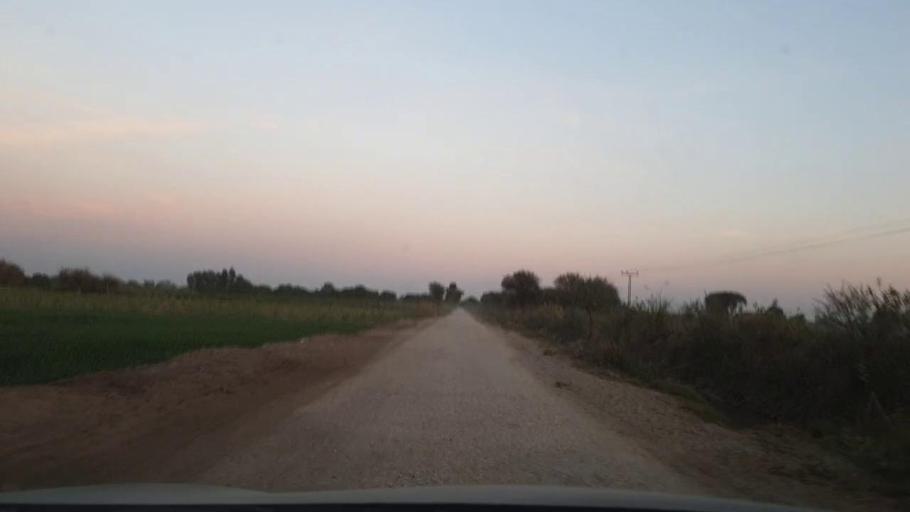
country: PK
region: Sindh
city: Tando Allahyar
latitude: 25.5568
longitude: 68.7828
